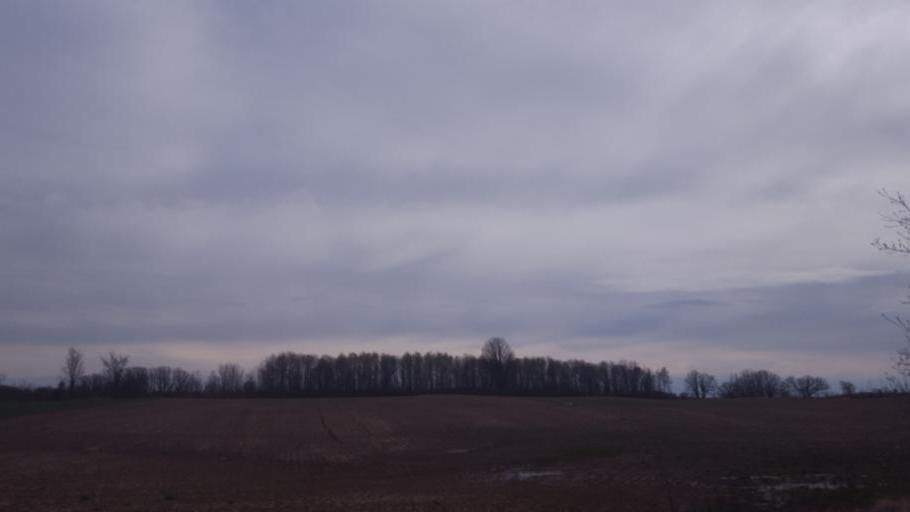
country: US
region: Michigan
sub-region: Clare County
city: Clare
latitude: 43.8730
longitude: -84.7181
